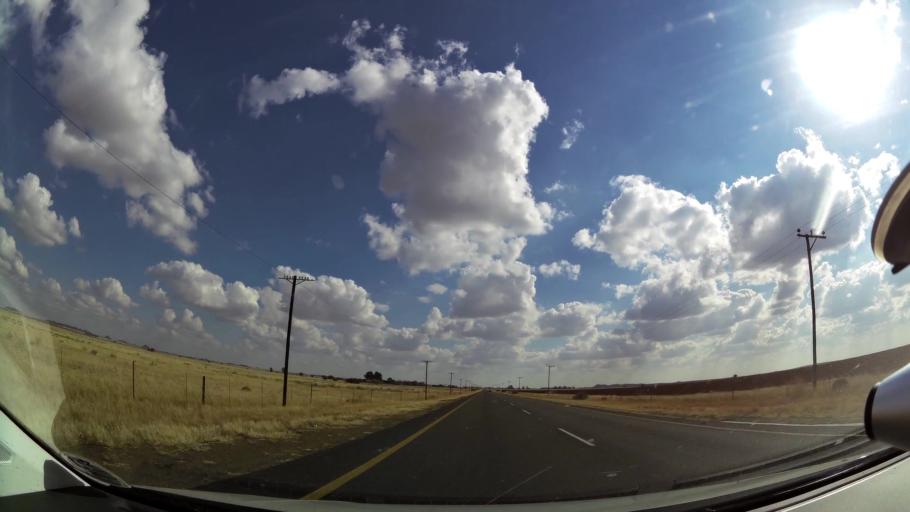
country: ZA
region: Orange Free State
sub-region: Xhariep District Municipality
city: Koffiefontein
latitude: -29.1289
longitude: 25.5001
